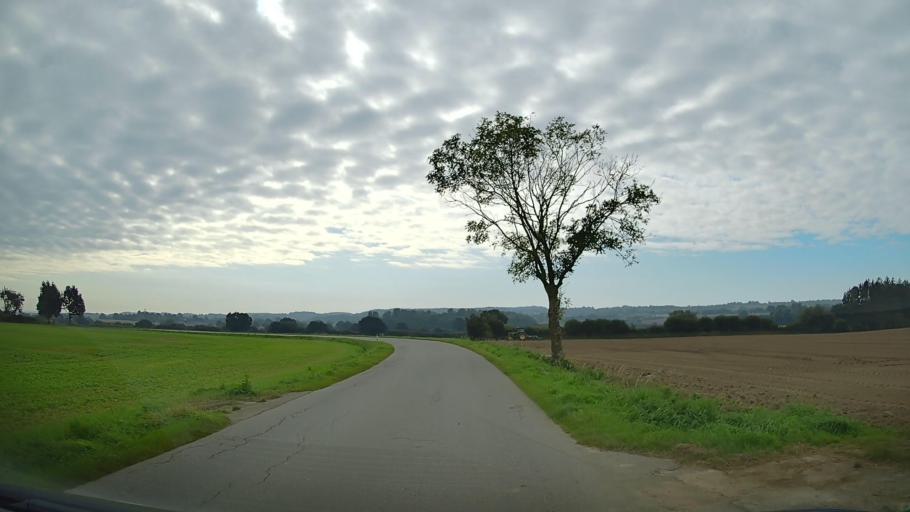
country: DE
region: Schleswig-Holstein
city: Panker
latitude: 54.3596
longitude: 10.5543
